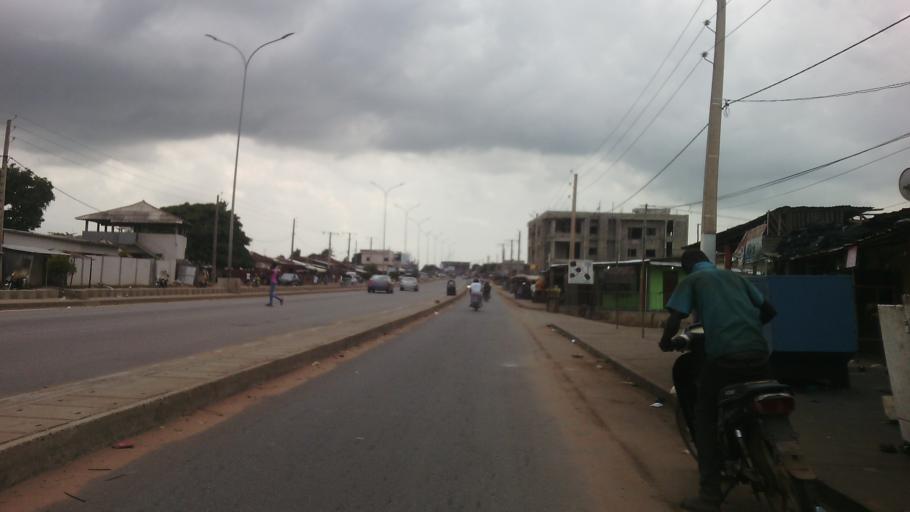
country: BJ
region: Atlantique
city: Abomey-Calavi
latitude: 6.4481
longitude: 2.3552
